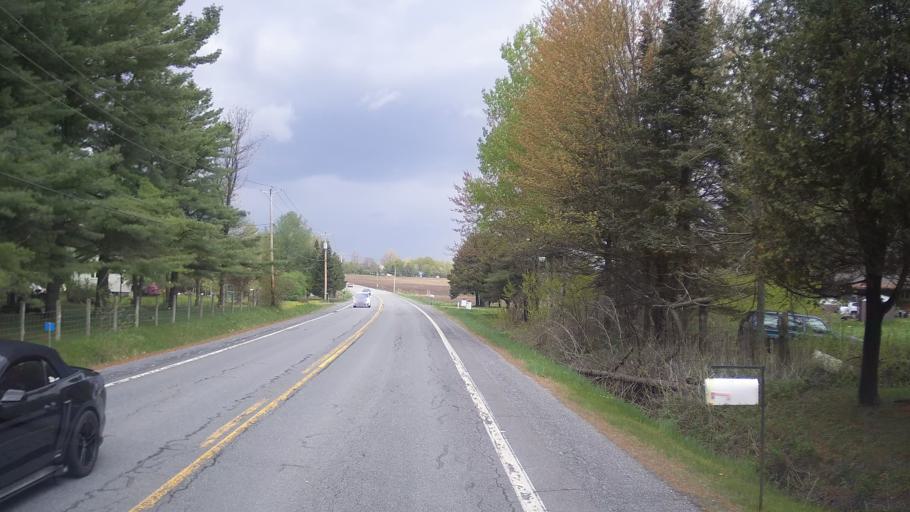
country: CA
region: Quebec
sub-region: Monteregie
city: Farnham
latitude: 45.2408
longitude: -72.8831
